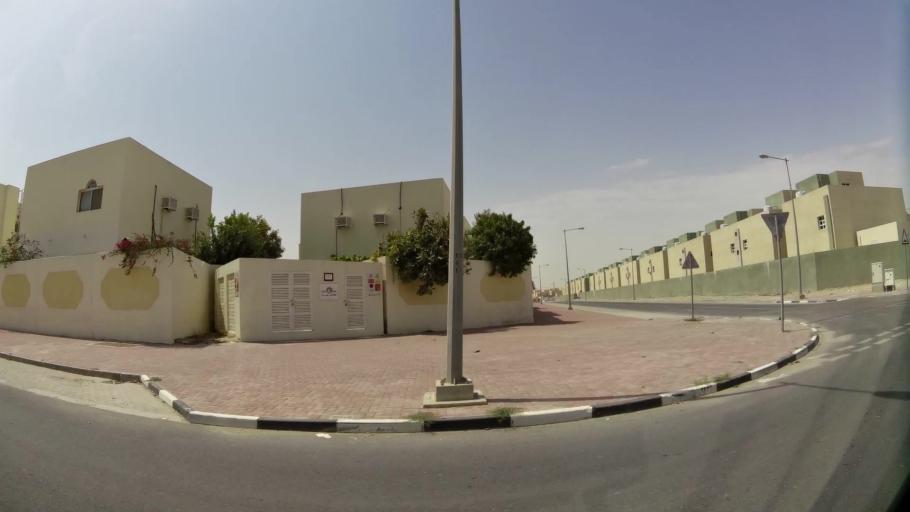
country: QA
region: Baladiyat ad Dawhah
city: Doha
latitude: 25.3285
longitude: 51.4888
